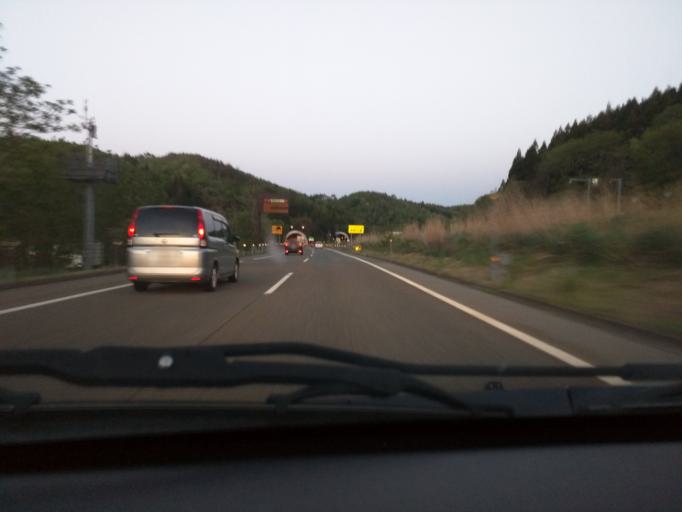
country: JP
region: Niigata
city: Kashiwazaki
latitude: 37.3388
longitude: 138.5330
